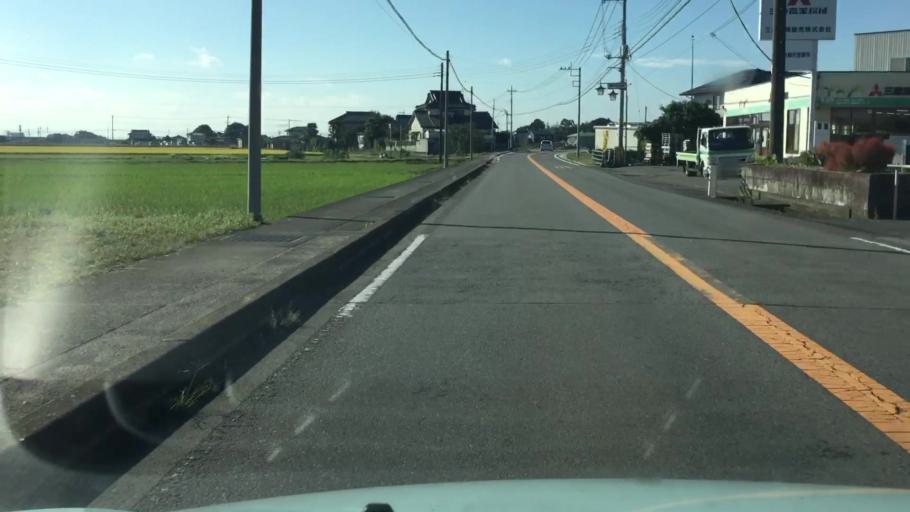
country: JP
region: Tochigi
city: Ujiie
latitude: 36.6525
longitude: 140.0211
